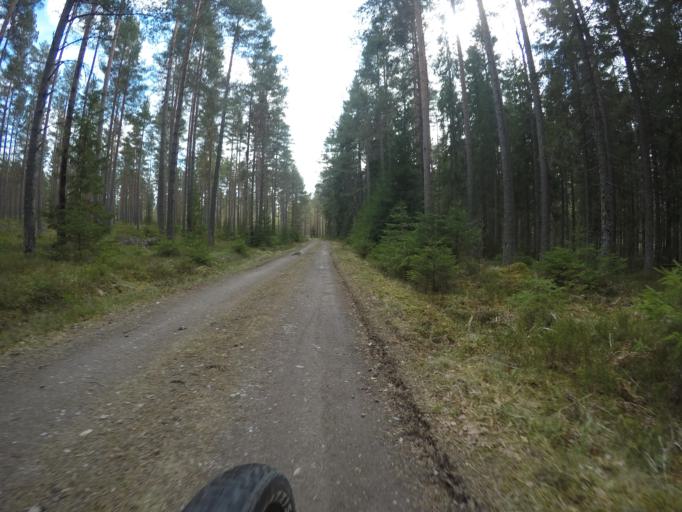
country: SE
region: Vaestmanland
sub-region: Kungsors Kommun
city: Kungsoer
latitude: 59.3400
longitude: 16.1070
